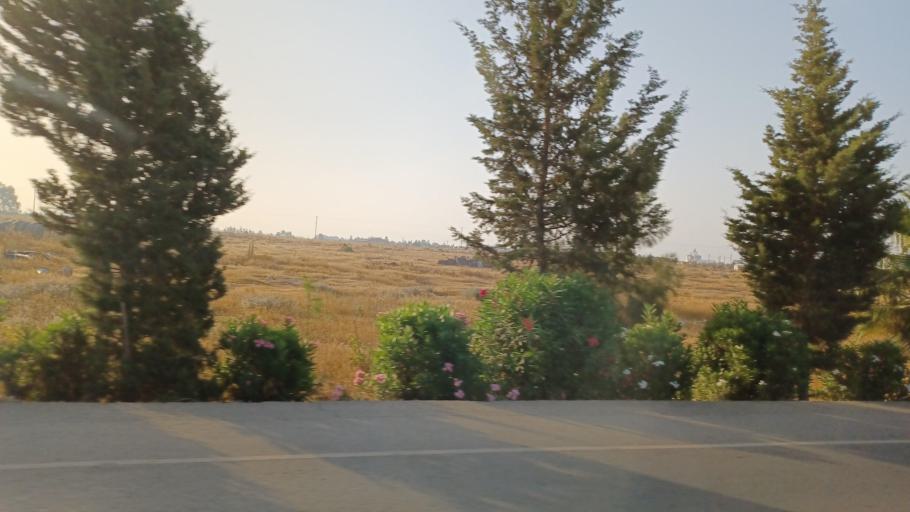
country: CY
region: Ammochostos
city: Frenaros
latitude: 35.0117
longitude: 33.9391
